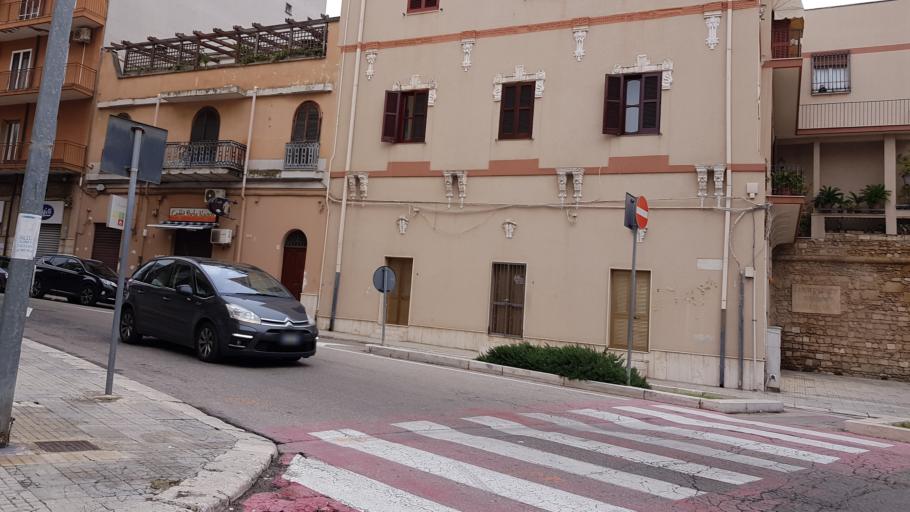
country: IT
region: Apulia
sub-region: Provincia di Brindisi
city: Brindisi
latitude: 40.6365
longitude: 17.9387
